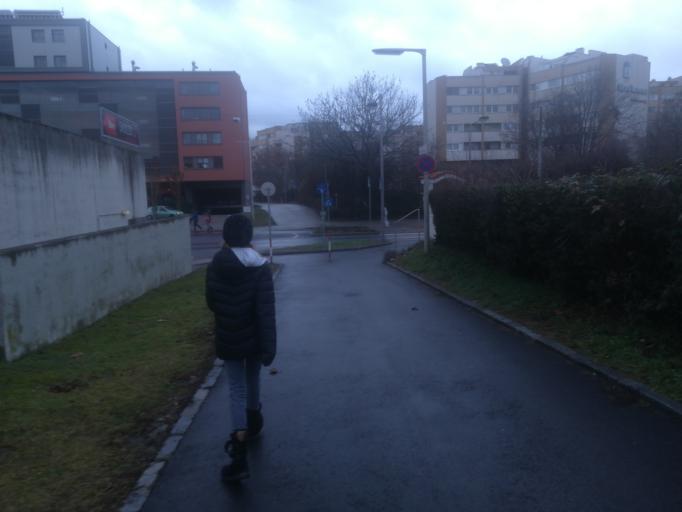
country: AT
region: Upper Austria
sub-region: Linz Stadt
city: Linz
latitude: 48.3305
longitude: 14.3137
